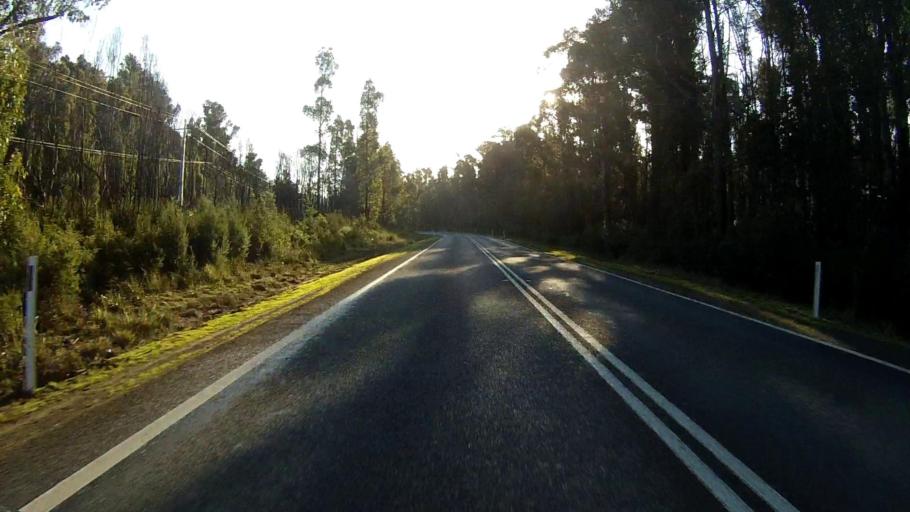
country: AU
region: Tasmania
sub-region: Sorell
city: Sorell
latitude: -42.9875
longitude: 147.9203
